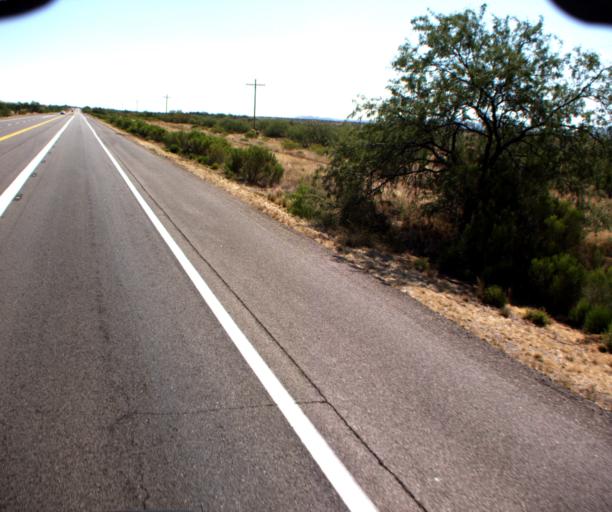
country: US
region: Arizona
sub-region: Pima County
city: Catalina
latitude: 32.5785
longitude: -110.9144
